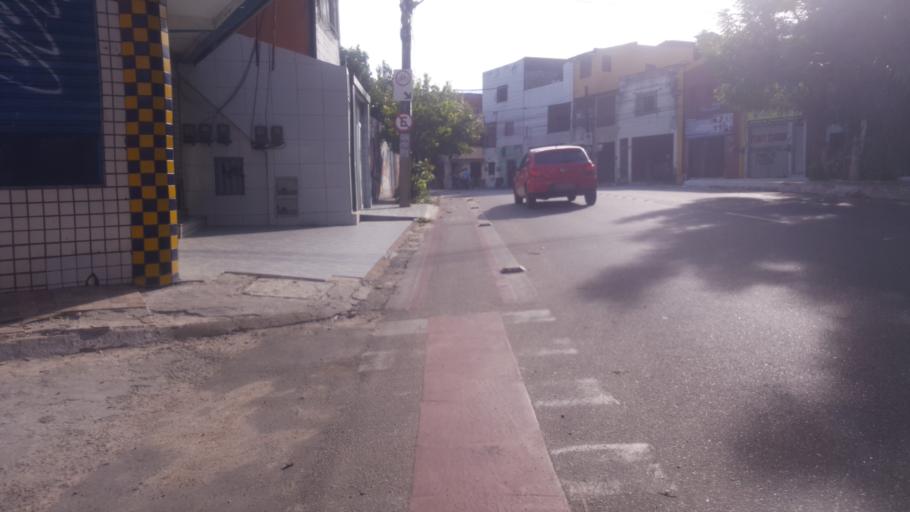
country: BR
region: Ceara
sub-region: Fortaleza
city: Fortaleza
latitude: -3.7548
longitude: -38.5405
